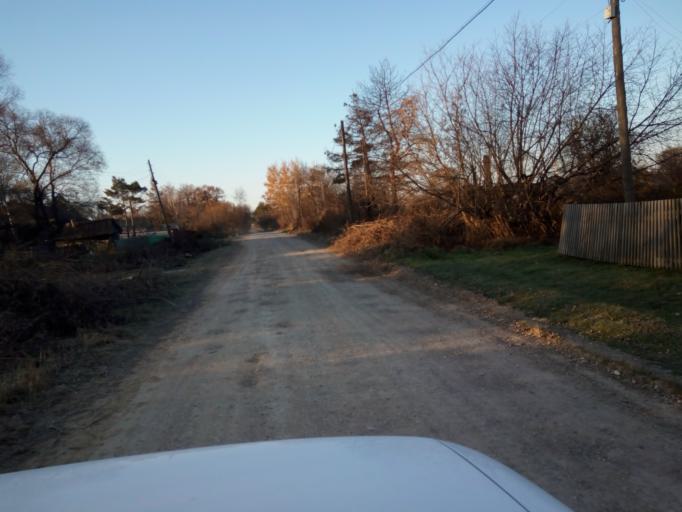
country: RU
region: Primorskiy
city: Lazo
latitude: 45.8779
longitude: 133.6514
